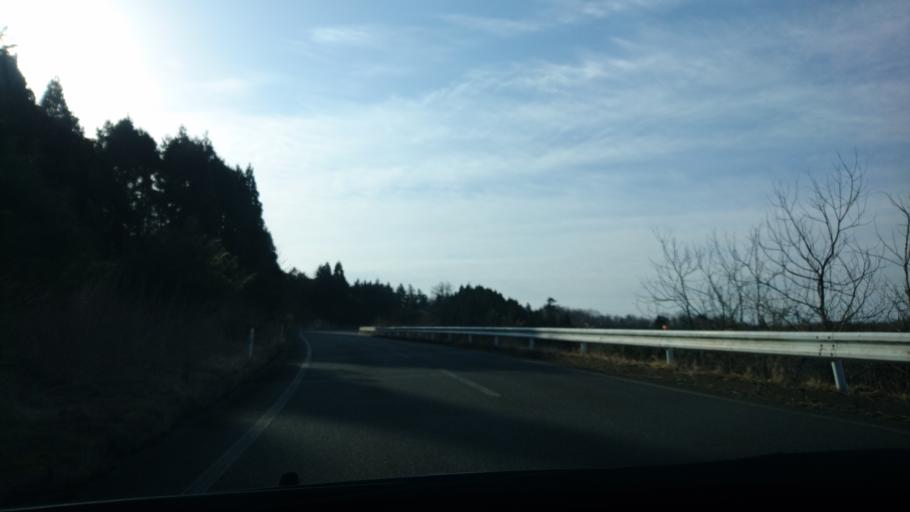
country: JP
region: Iwate
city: Ichinoseki
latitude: 38.8590
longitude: 141.1993
